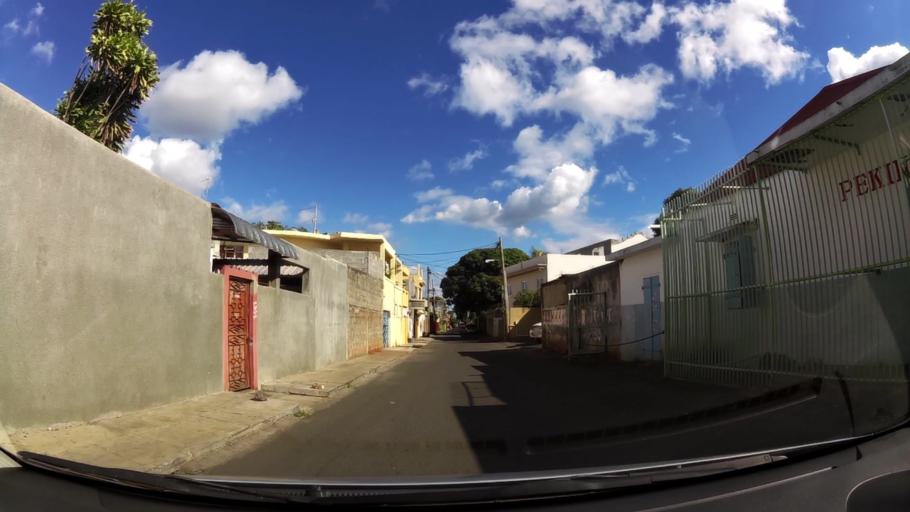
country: MU
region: Pamplemousses
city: Le Hochet
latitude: -20.1441
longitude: 57.5192
